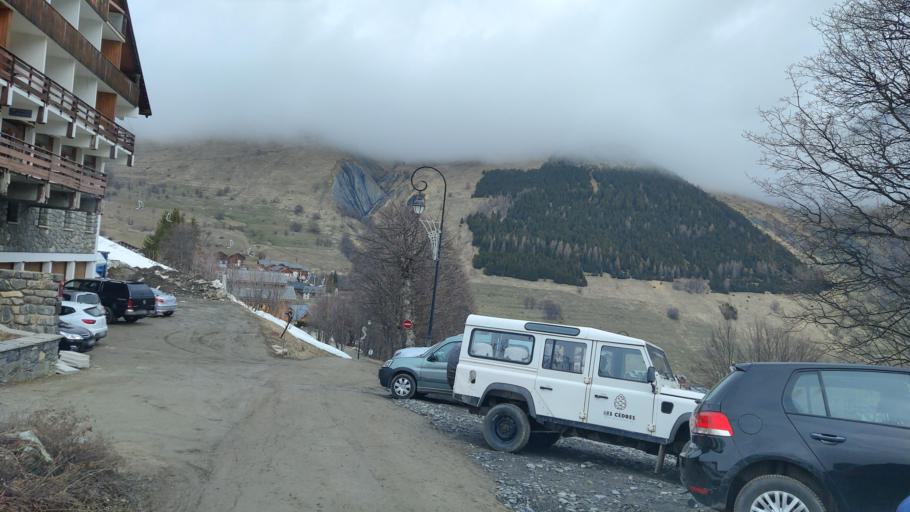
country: FR
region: Rhone-Alpes
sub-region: Departement de la Savoie
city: Saint-Jean-de-Maurienne
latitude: 45.2162
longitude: 6.2255
